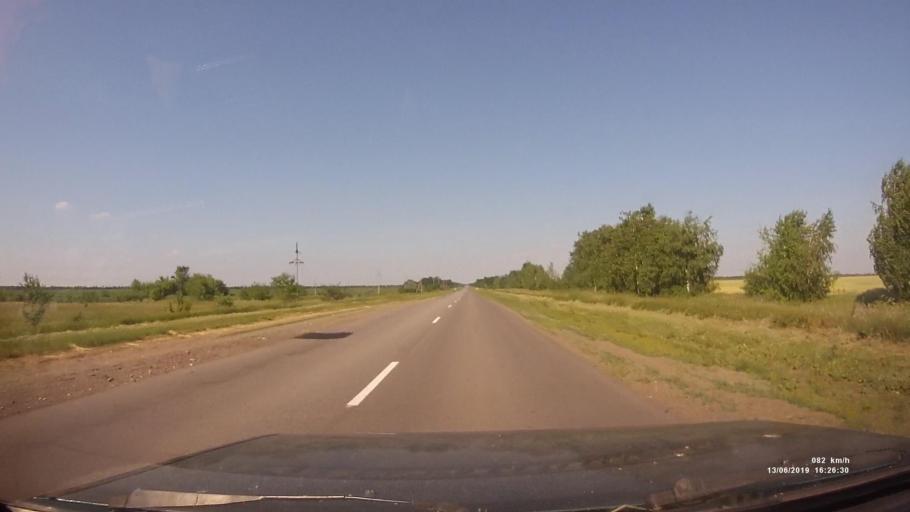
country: RU
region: Rostov
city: Kazanskaya
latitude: 49.8055
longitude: 41.1667
